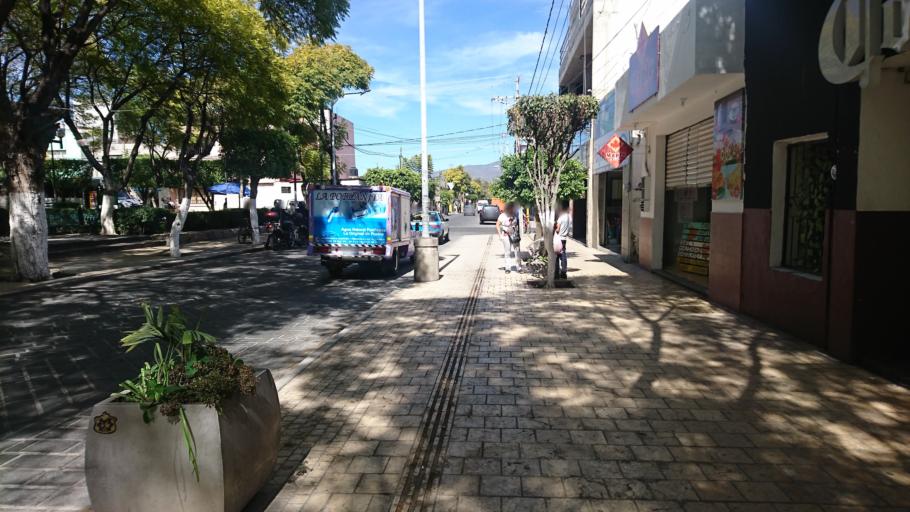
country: MX
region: Puebla
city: Tehuacan
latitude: 18.4667
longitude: -97.3930
